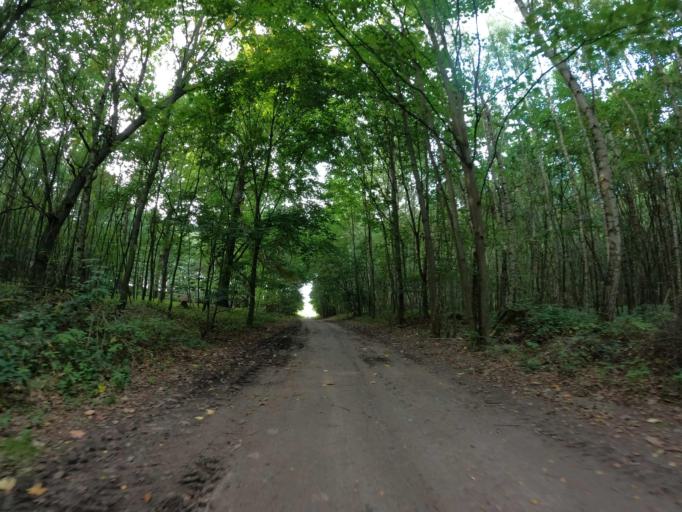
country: DE
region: Mecklenburg-Vorpommern
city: Klink
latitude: 53.4433
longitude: 12.5257
